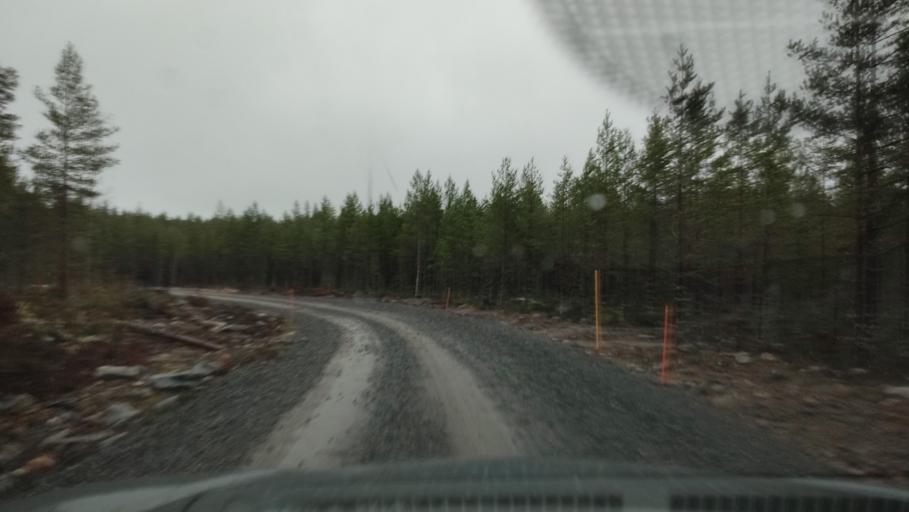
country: FI
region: Southern Ostrobothnia
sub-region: Suupohja
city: Karijoki
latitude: 62.1476
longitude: 21.6259
